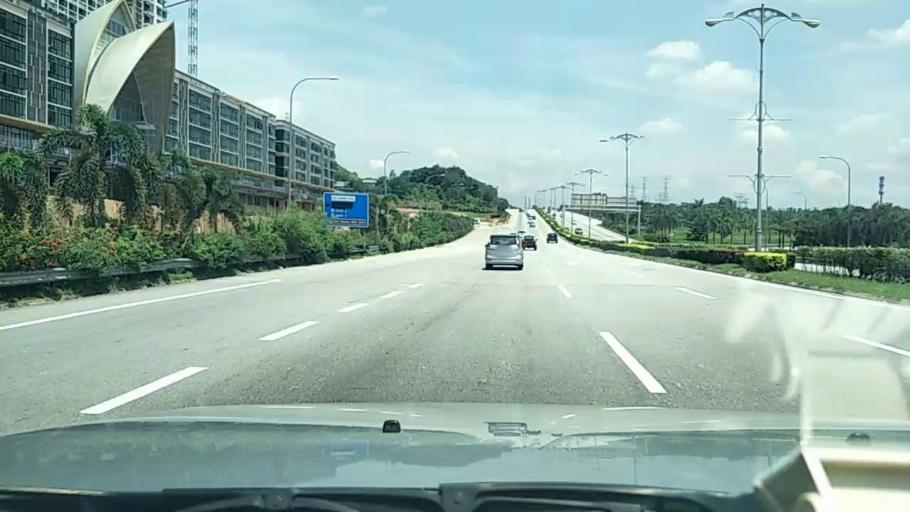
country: MY
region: Putrajaya
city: Putrajaya
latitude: 2.9670
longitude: 101.7198
